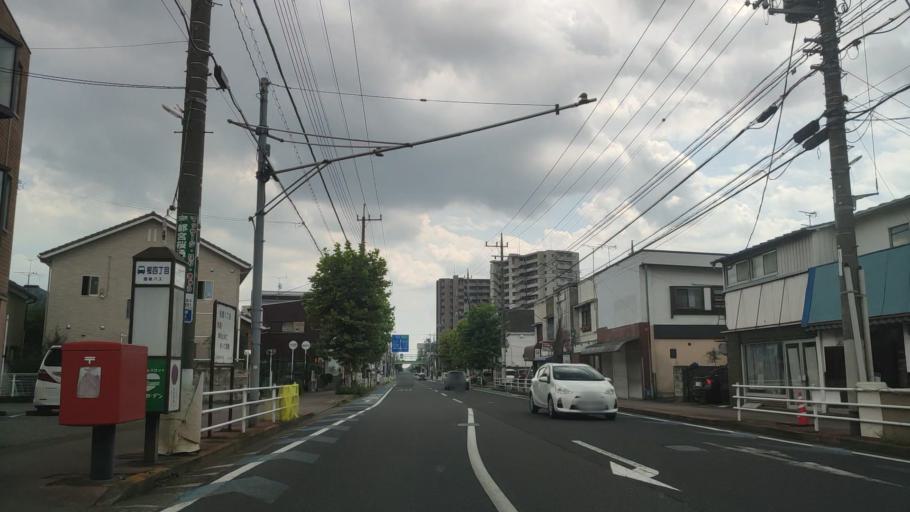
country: JP
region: Tochigi
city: Utsunomiya-shi
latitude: 36.5694
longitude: 139.8692
